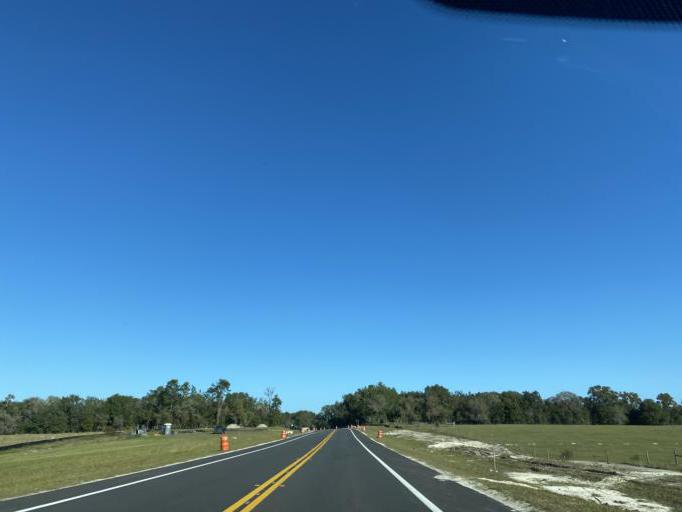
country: US
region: Florida
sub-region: Lake County
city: Mount Plymouth
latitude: 28.8263
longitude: -81.5214
